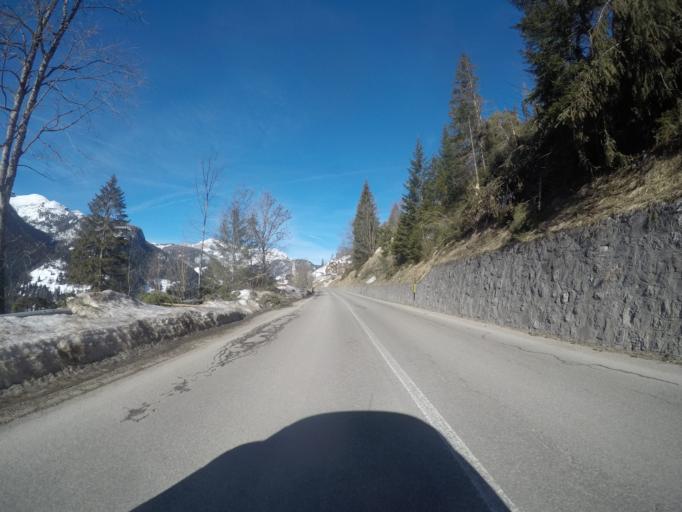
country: IT
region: Veneto
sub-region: Provincia di Belluno
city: Livinallongo del Col di Lana
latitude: 46.4781
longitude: 11.9612
